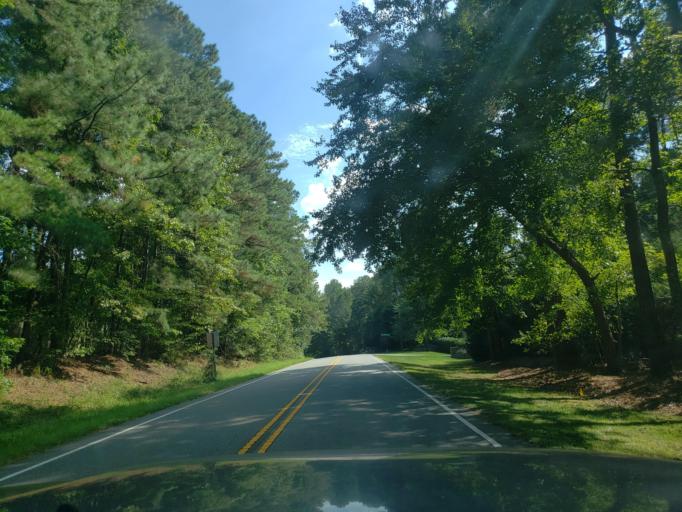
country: US
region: North Carolina
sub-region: Wake County
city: West Raleigh
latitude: 35.9369
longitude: -78.6942
